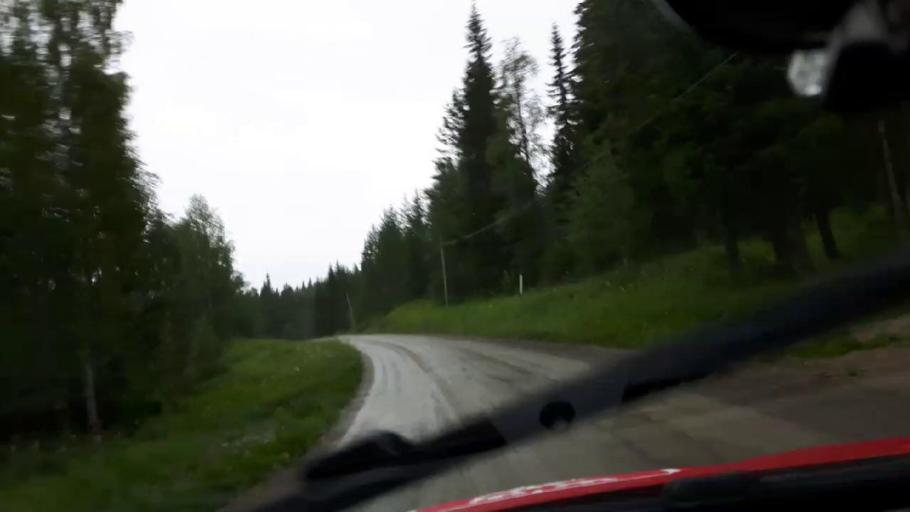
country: SE
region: Jaemtland
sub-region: OEstersunds Kommun
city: Brunflo
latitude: 62.8848
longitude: 14.8749
